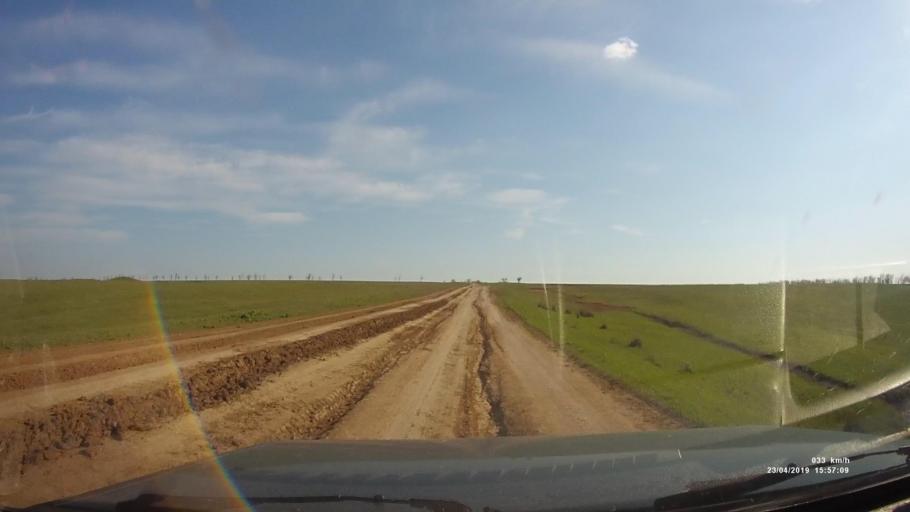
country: RU
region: Rostov
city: Remontnoye
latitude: 46.5335
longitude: 43.1098
